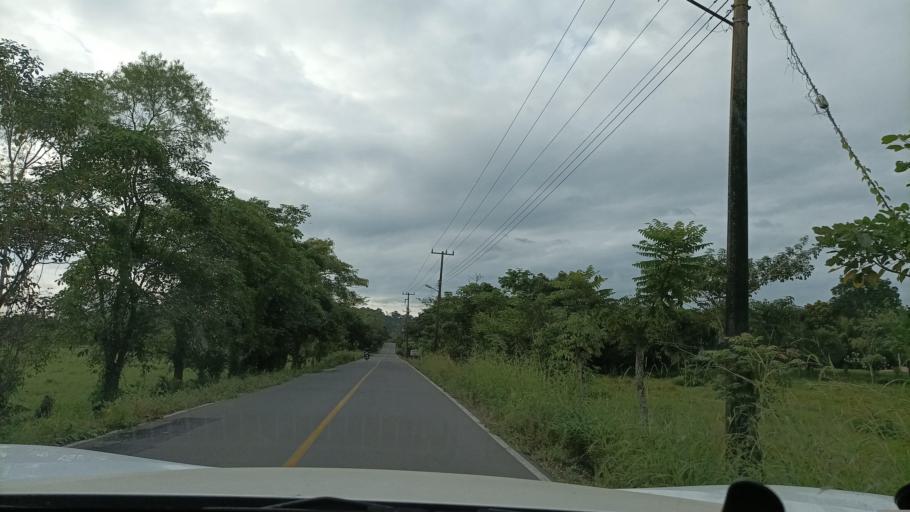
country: MX
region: Veracruz
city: Hidalgotitlan
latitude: 17.7253
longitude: -94.4821
